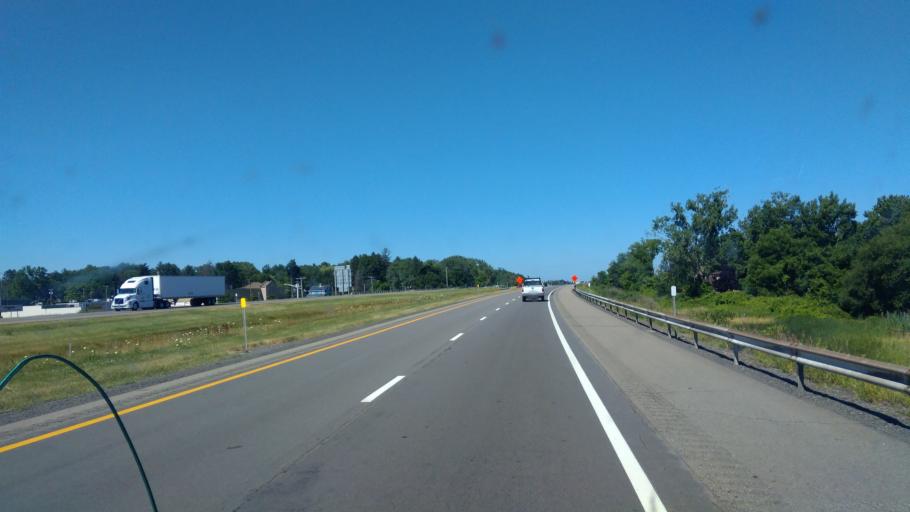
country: US
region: New York
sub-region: Chautauqua County
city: Fredonia
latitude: 42.4595
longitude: -79.3304
